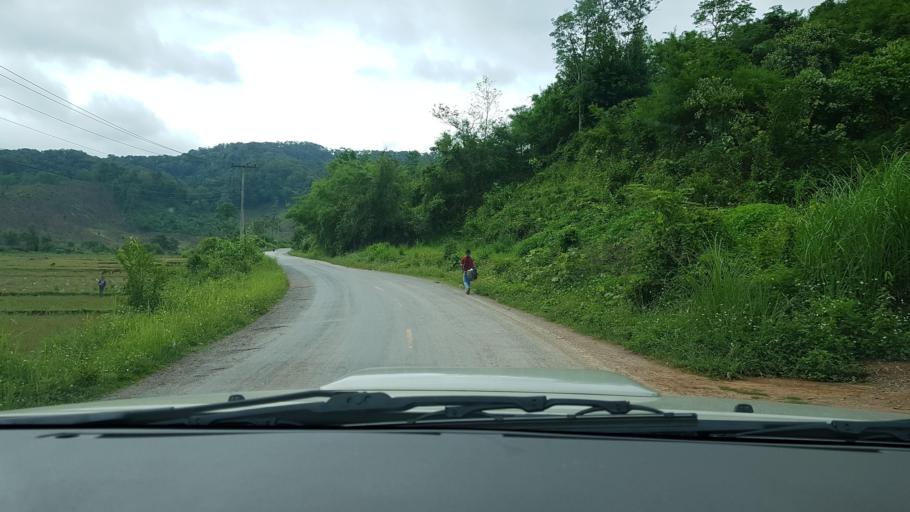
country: LA
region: Oudomxai
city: Muang Xay
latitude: 20.5792
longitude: 101.9208
